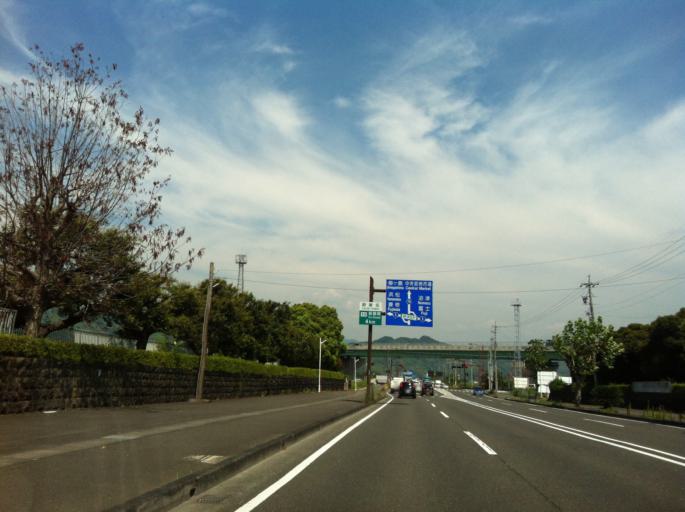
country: JP
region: Shizuoka
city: Shizuoka-shi
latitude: 35.0069
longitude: 138.4031
